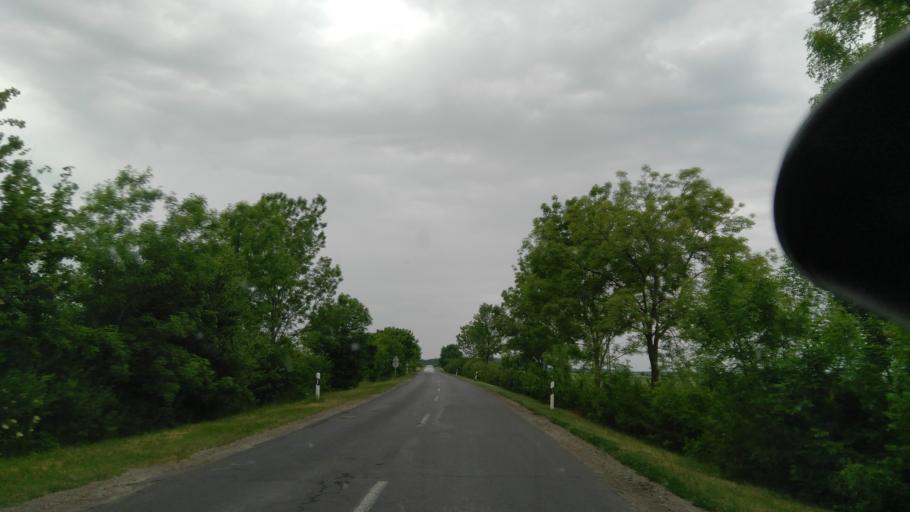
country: HU
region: Bekes
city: Doboz
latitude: 46.7256
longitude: 21.2935
